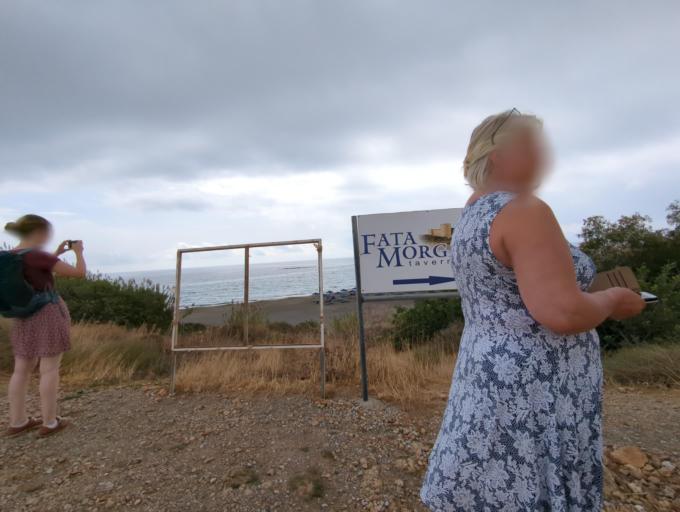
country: GR
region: Crete
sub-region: Nomos Chanias
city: Chora Sfakion
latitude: 35.1817
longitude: 24.2346
